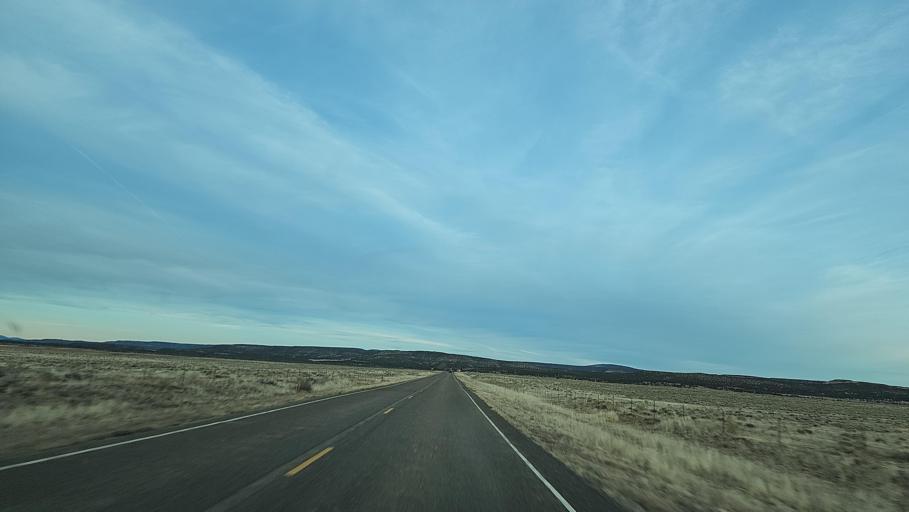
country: US
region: New Mexico
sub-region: Cibola County
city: Grants
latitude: 34.7064
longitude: -108.0157
